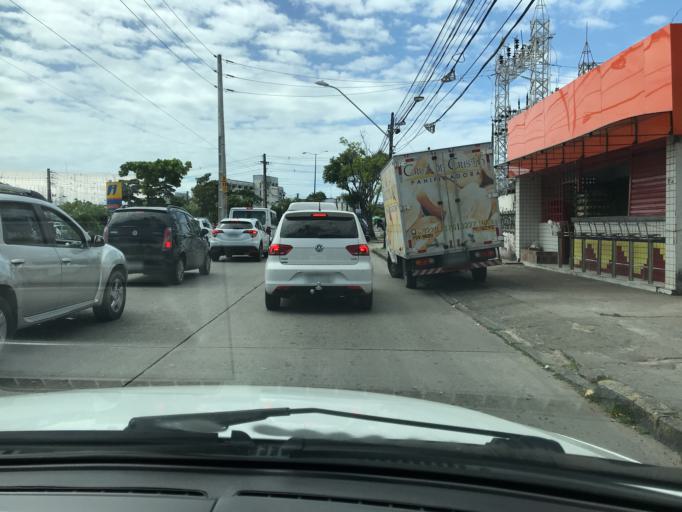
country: BR
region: Pernambuco
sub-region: Recife
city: Recife
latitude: -8.0613
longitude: -34.9058
